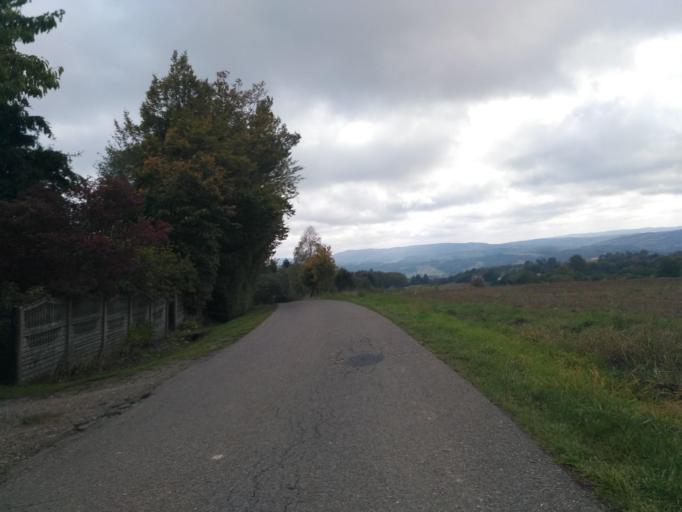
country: PL
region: Subcarpathian Voivodeship
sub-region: Powiat ropczycko-sedziszowski
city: Niedzwiada
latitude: 49.9546
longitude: 21.4559
